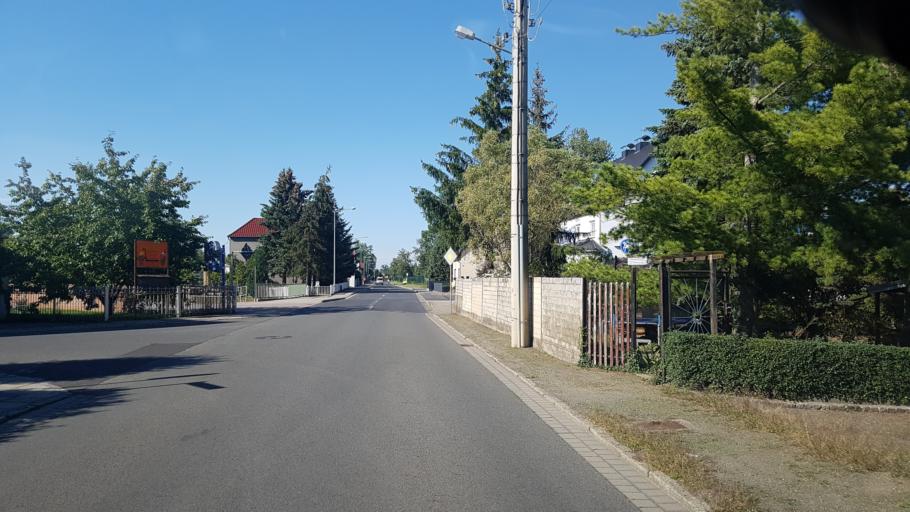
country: DE
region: Brandenburg
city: Lauchhammer
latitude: 51.4771
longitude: 13.7355
